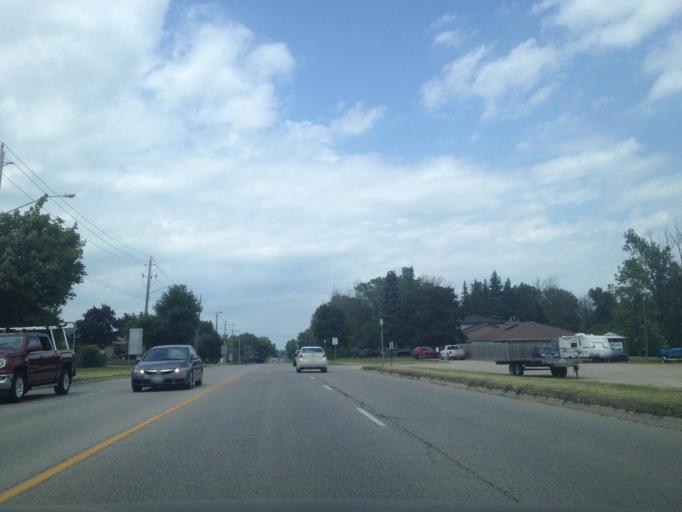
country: CA
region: Ontario
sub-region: Wellington County
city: Guelph
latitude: 43.5751
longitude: -80.2468
